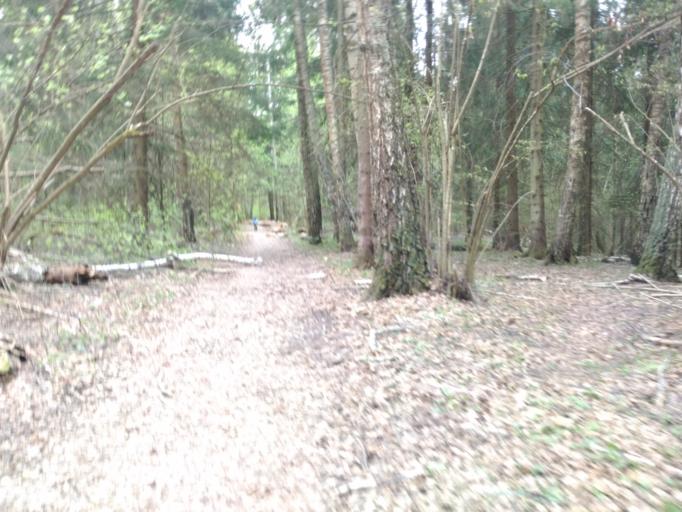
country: RU
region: Moskovskaya
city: Dedovsk
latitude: 55.8445
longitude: 37.1004
